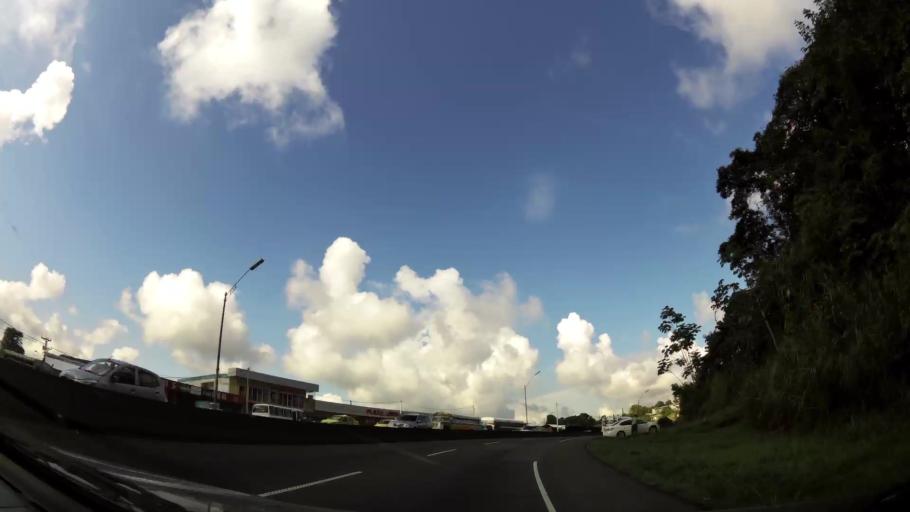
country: PA
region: Panama
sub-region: Distrito Arraijan
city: Arraijan
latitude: 8.9508
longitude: -79.6329
